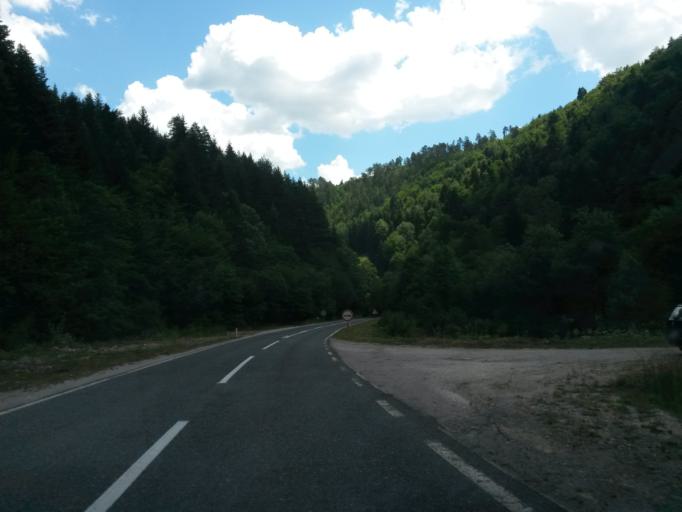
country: BA
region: Federation of Bosnia and Herzegovina
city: Bugojno
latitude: 44.0262
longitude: 17.3608
